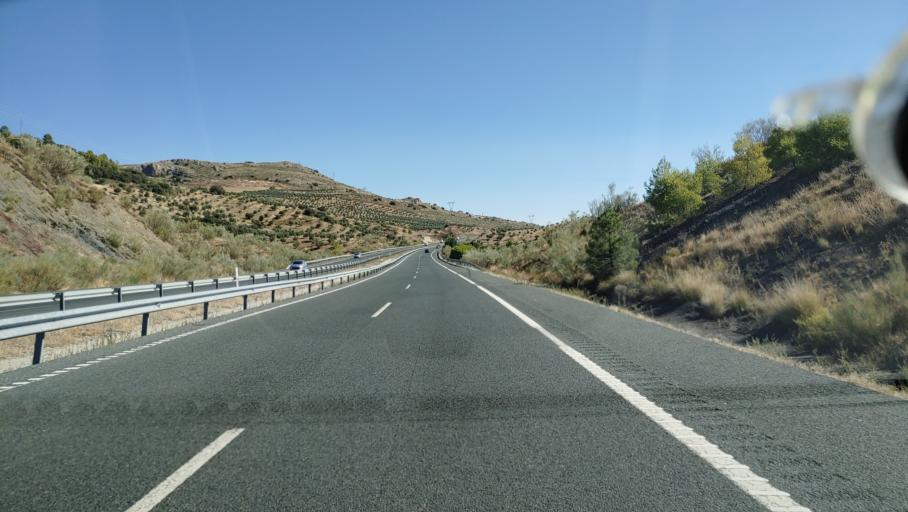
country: ES
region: Andalusia
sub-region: Provincia de Granada
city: Diezma
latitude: 37.3084
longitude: -3.3637
